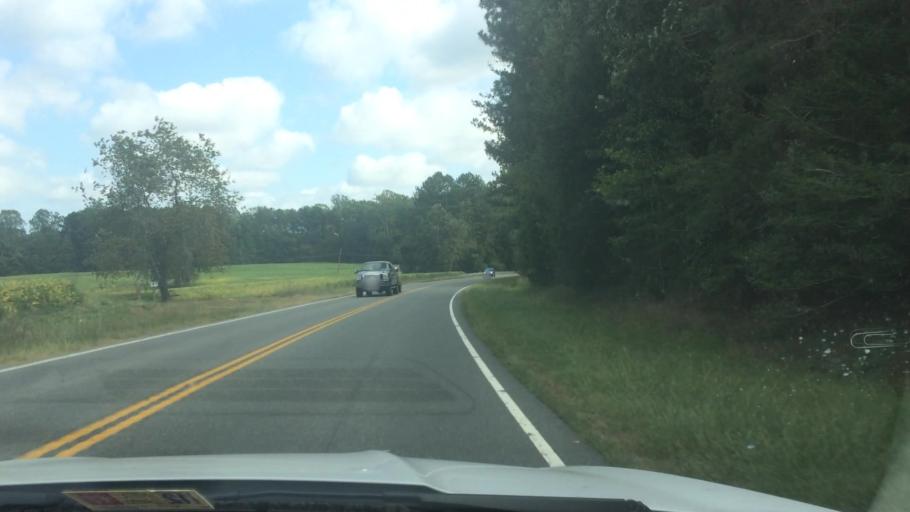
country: US
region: Virginia
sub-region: Northumberland County
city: Heathsville
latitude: 37.8513
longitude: -76.5868
